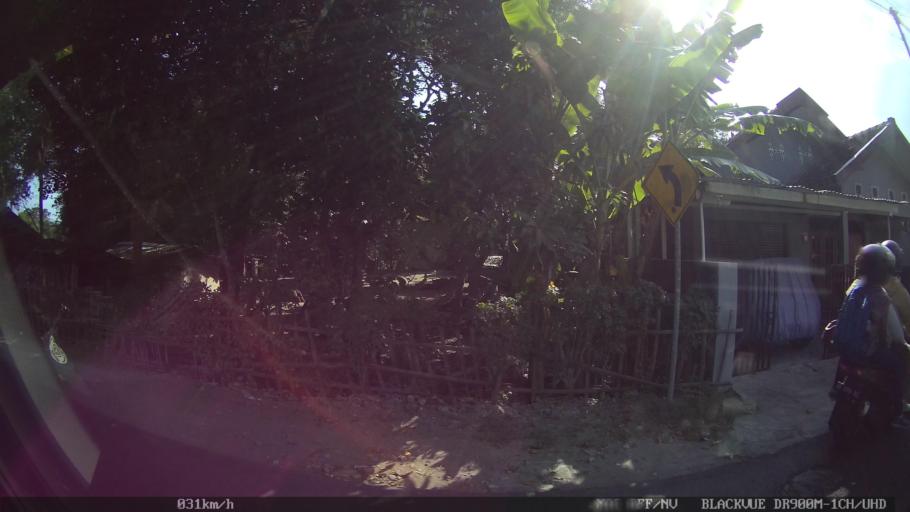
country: ID
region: Daerah Istimewa Yogyakarta
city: Kasihan
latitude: -7.8303
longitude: 110.3383
